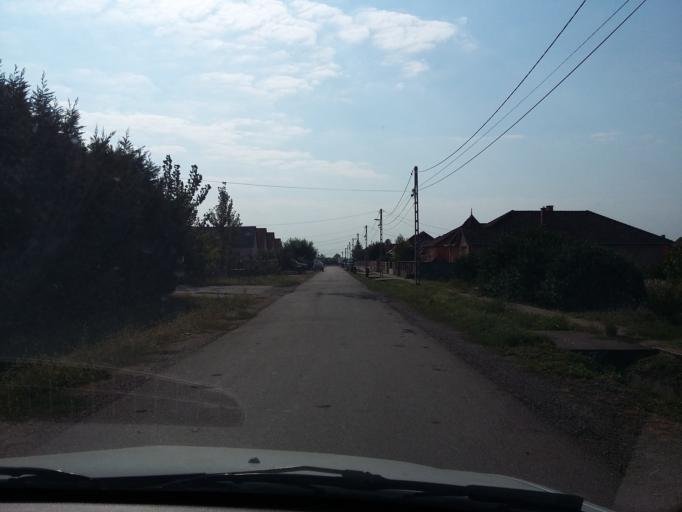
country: HU
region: Borsod-Abauj-Zemplen
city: Bekecs
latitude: 48.1528
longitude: 21.1827
